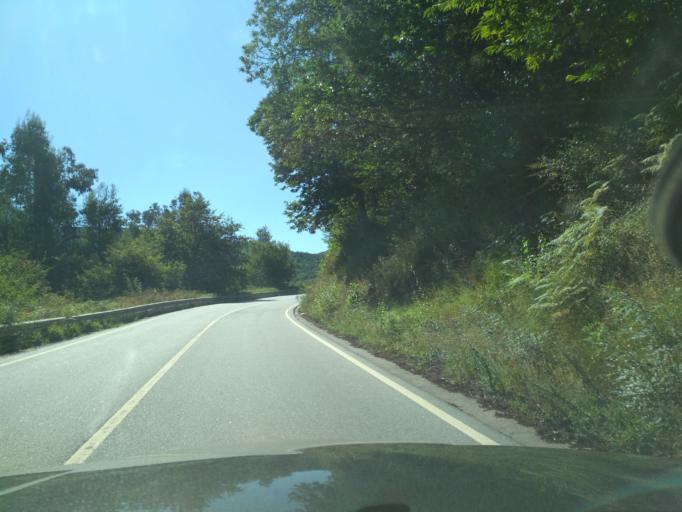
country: PT
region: Vila Real
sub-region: Ribeira de Pena
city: Ribeira de Pena
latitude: 41.5106
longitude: -7.7943
